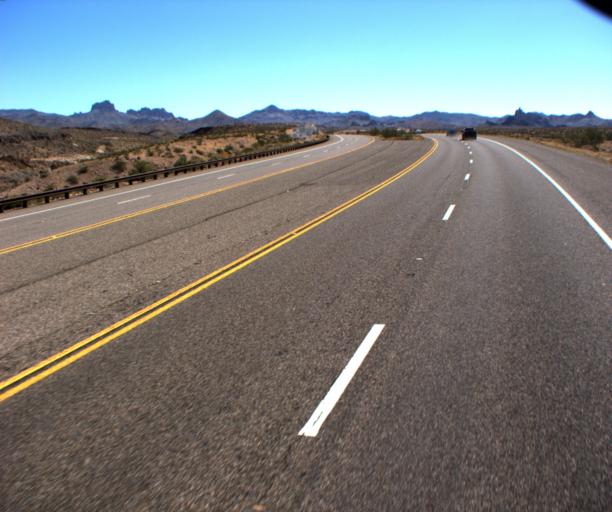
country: US
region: Nevada
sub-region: Clark County
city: Laughlin
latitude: 35.1846
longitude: -114.4970
